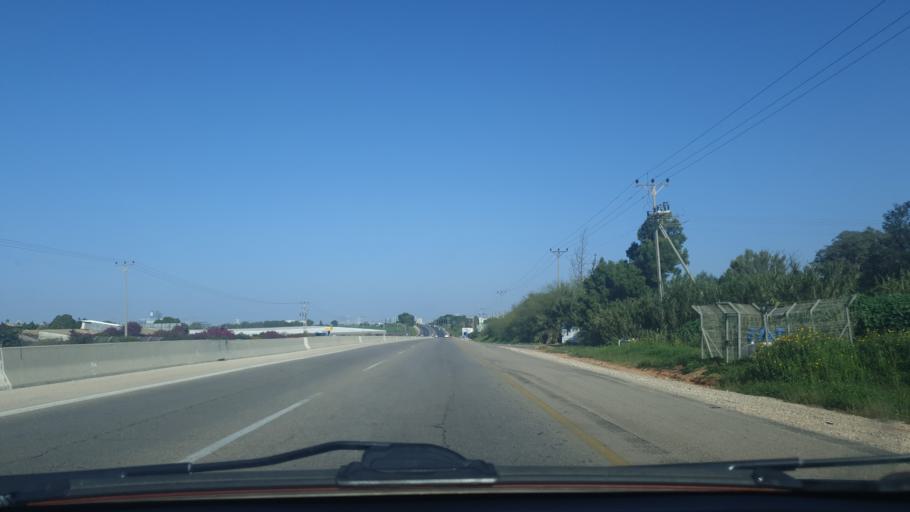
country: IL
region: Central District
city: Bet Dagan
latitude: 31.9865
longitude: 34.8316
